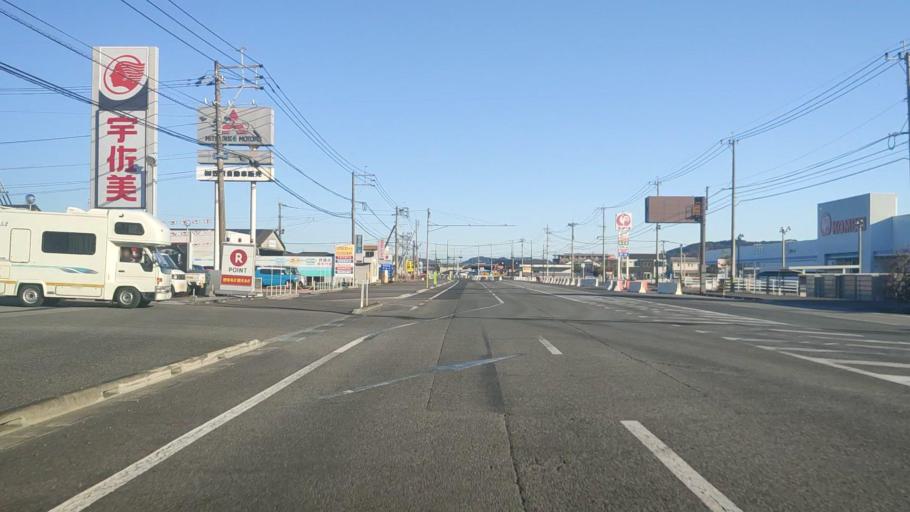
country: JP
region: Miyazaki
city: Nobeoka
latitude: 32.3999
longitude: 131.6303
